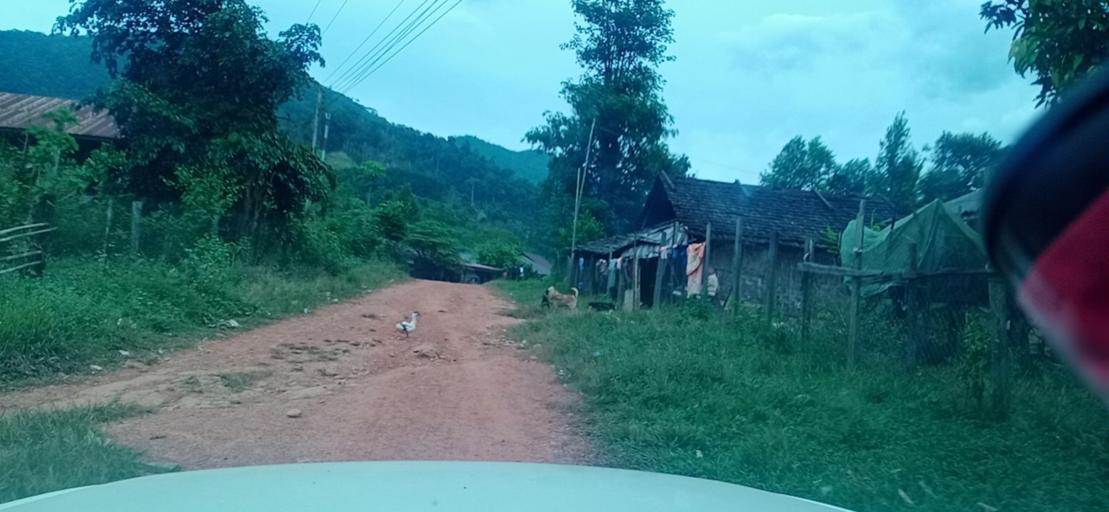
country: TH
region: Changwat Bueng Kan
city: Pak Khat
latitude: 18.5676
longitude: 103.3094
